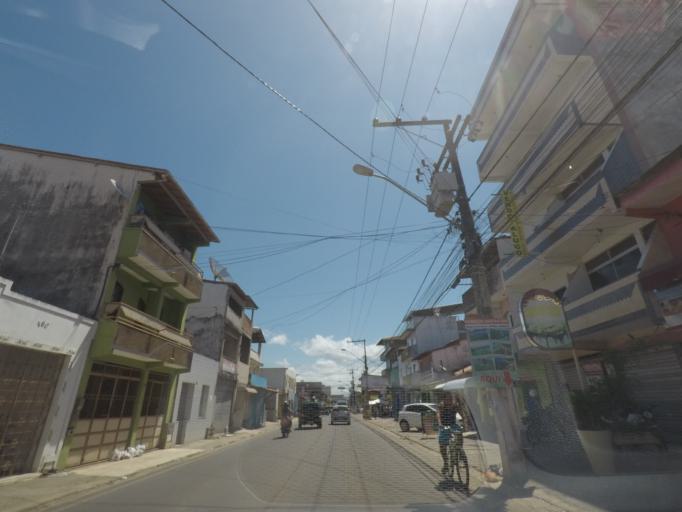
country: BR
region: Bahia
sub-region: Valenca
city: Valenca
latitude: -13.3647
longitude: -39.0693
